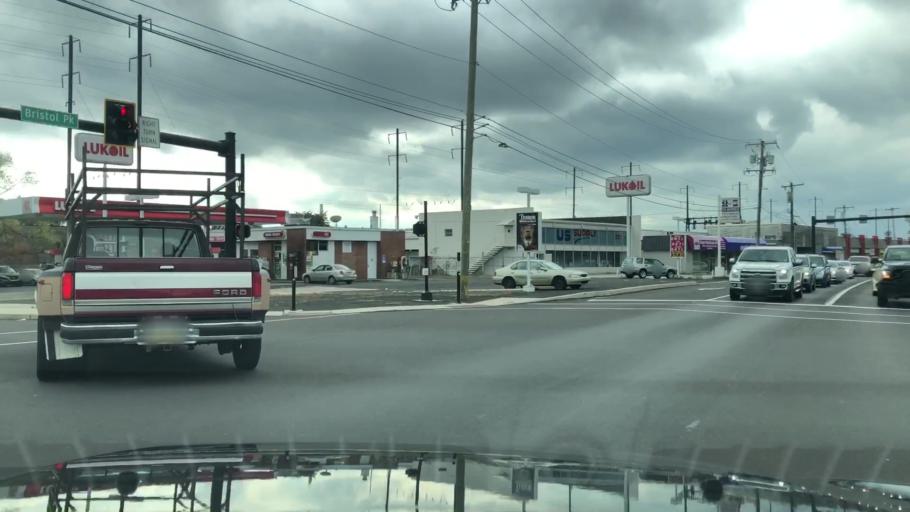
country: US
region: Pennsylvania
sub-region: Bucks County
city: Bristol
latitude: 40.1021
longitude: -74.8633
